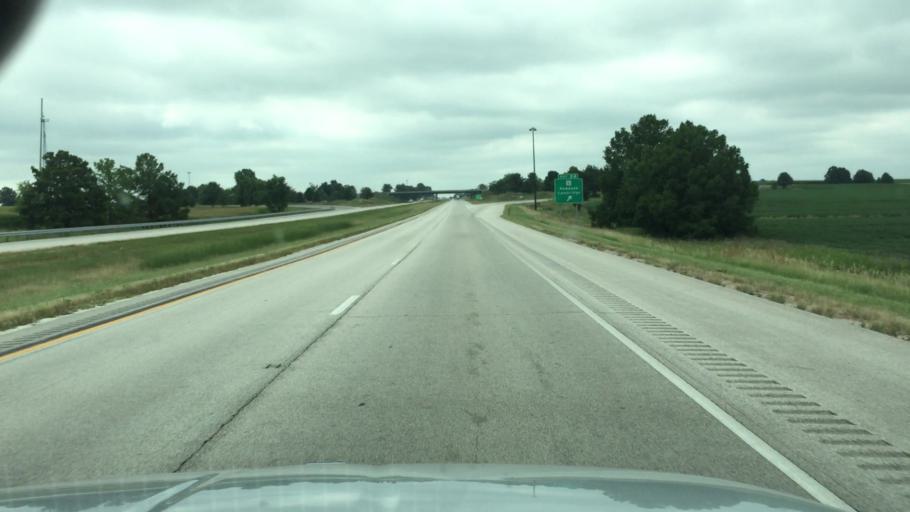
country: US
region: Illinois
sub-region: Henry County
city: Orion
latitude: 41.3012
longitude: -90.3342
